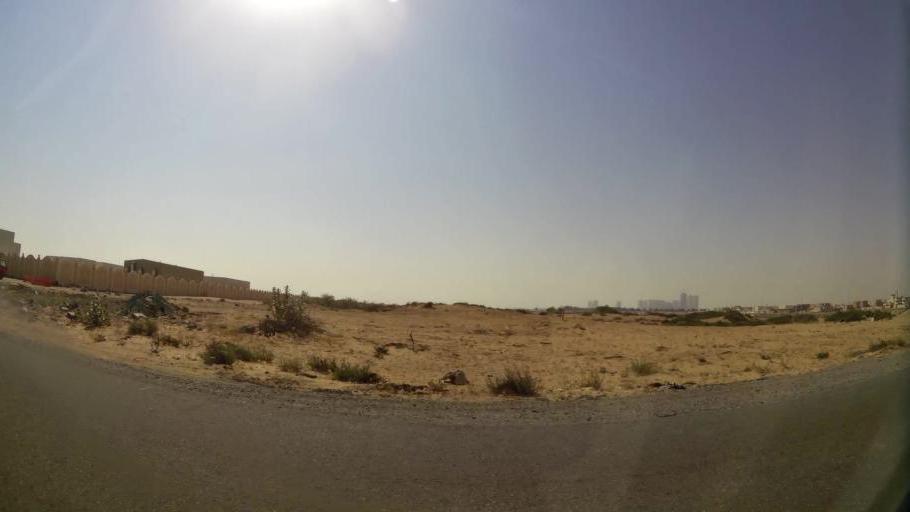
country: AE
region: Ajman
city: Ajman
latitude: 25.4183
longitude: 55.5496
